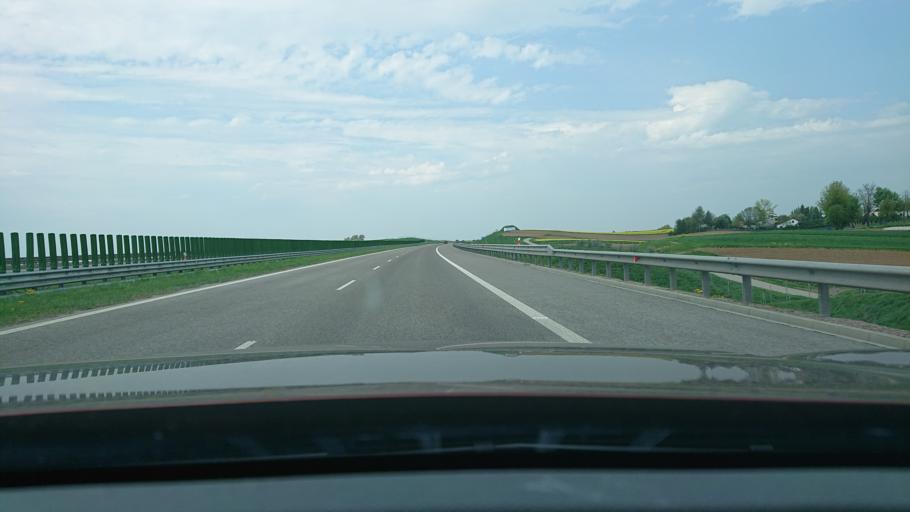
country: PL
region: Subcarpathian Voivodeship
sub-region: Powiat jaroslawski
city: Pawlosiow
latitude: 49.9500
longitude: 22.6636
